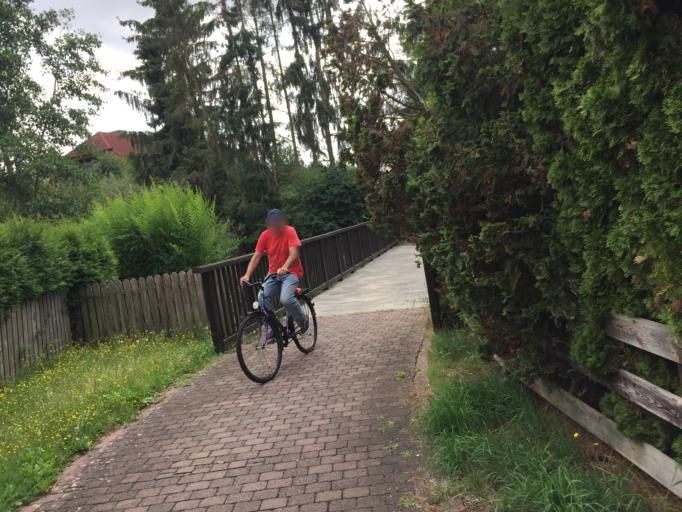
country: DE
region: Hesse
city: Schwalmstadt
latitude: 50.9143
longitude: 9.2354
